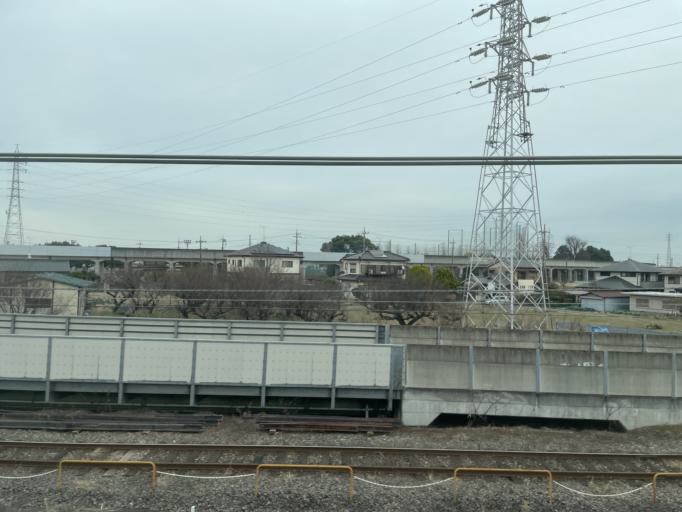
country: JP
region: Saitama
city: Kukichuo
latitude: 36.0814
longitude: 139.6801
